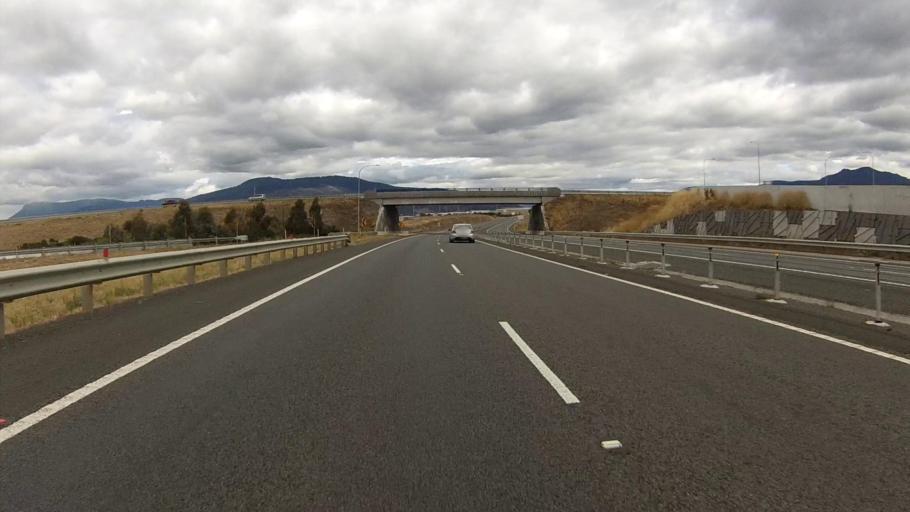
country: AU
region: Tasmania
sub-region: Brighton
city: Bridgewater
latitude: -42.7132
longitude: 147.2464
